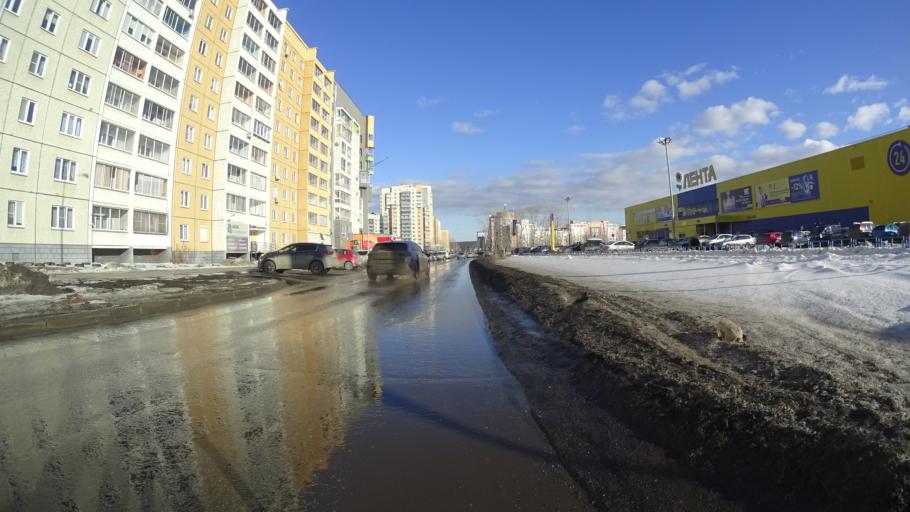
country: RU
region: Chelyabinsk
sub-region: Gorod Chelyabinsk
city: Chelyabinsk
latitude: 55.1600
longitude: 61.2926
